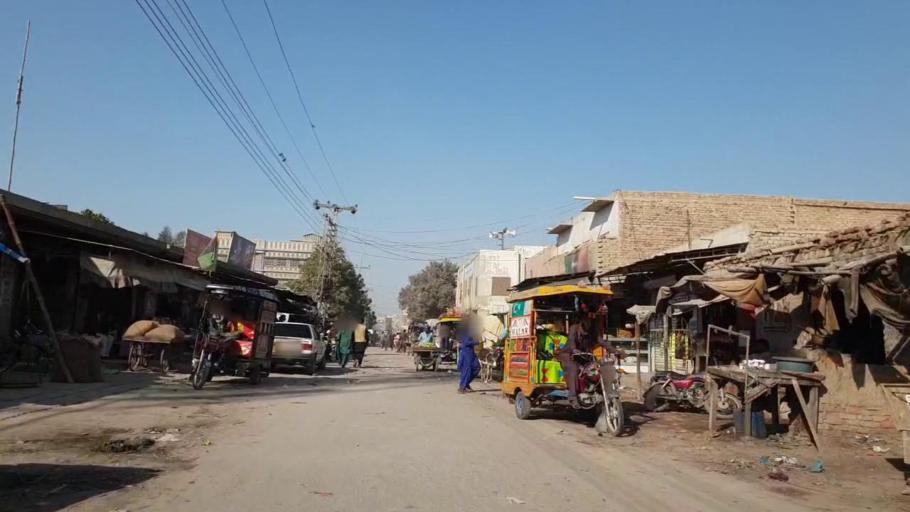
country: PK
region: Sindh
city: Digri
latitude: 25.1521
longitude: 69.1116
